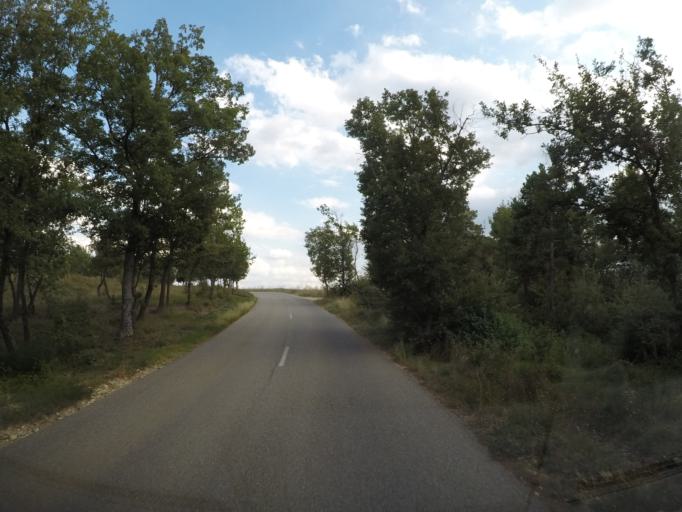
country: FR
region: Provence-Alpes-Cote d'Azur
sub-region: Departement des Alpes-de-Haute-Provence
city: Valensole
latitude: 43.8313
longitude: 6.0299
